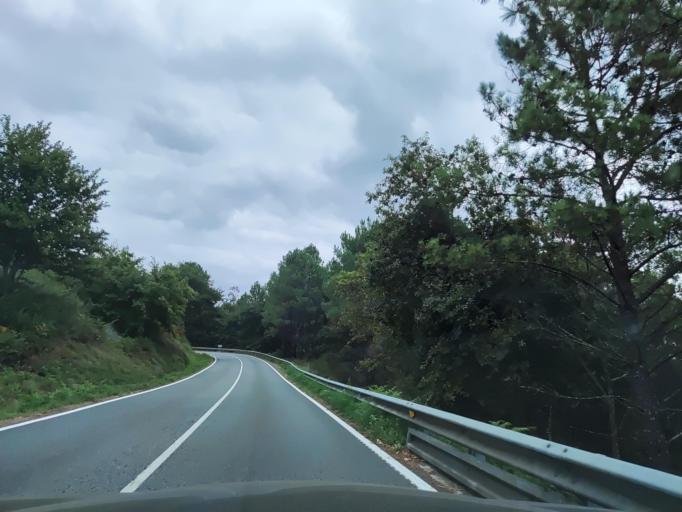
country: ES
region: Galicia
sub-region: Provincia da Coruna
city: Padron
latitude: 42.7462
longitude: -8.6165
